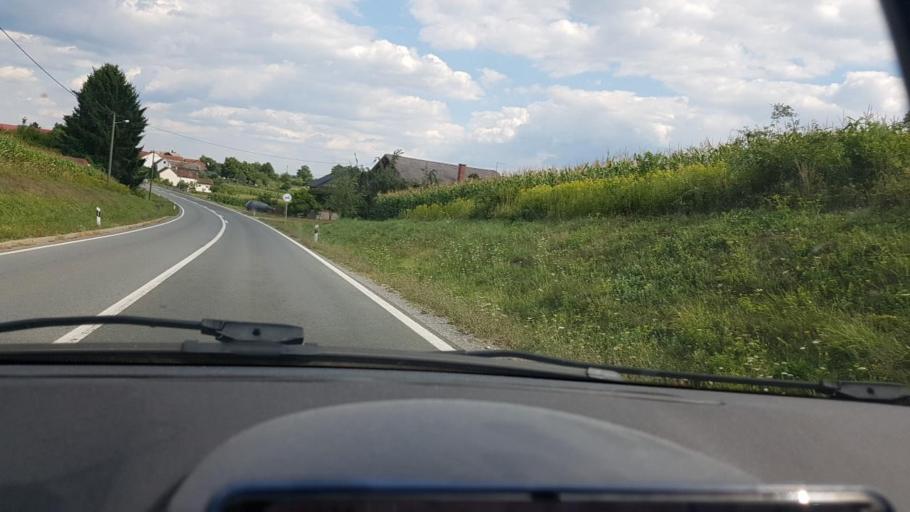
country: HR
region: Bjelovarsko-Bilogorska
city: Zdralovi
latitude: 45.8688
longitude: 16.9046
